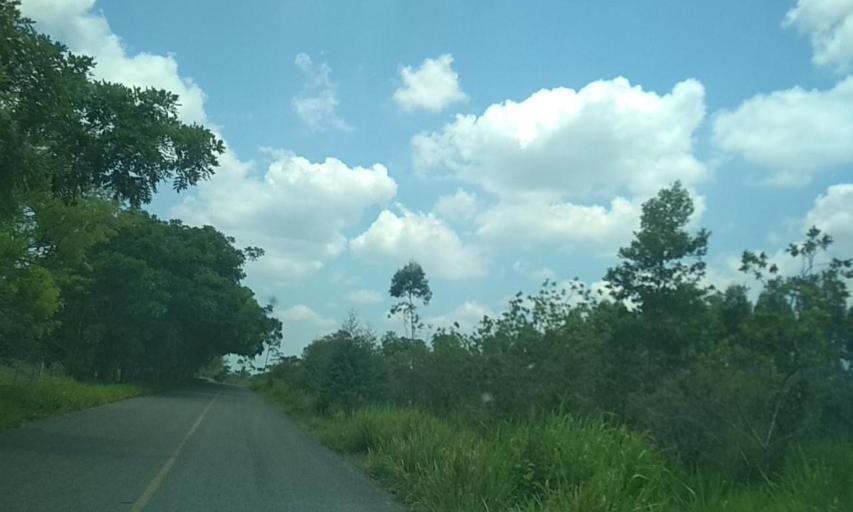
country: MX
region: Tabasco
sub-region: Huimanguillo
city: Francisco Rueda
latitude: 17.7916
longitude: -93.8480
